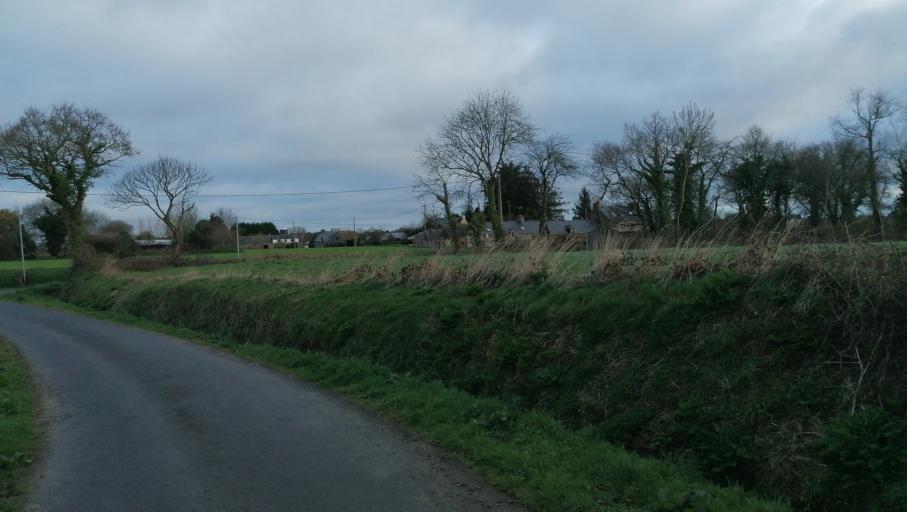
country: FR
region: Brittany
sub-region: Departement des Cotes-d'Armor
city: Pommerit-le-Vicomte
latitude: 48.6445
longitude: -3.0682
